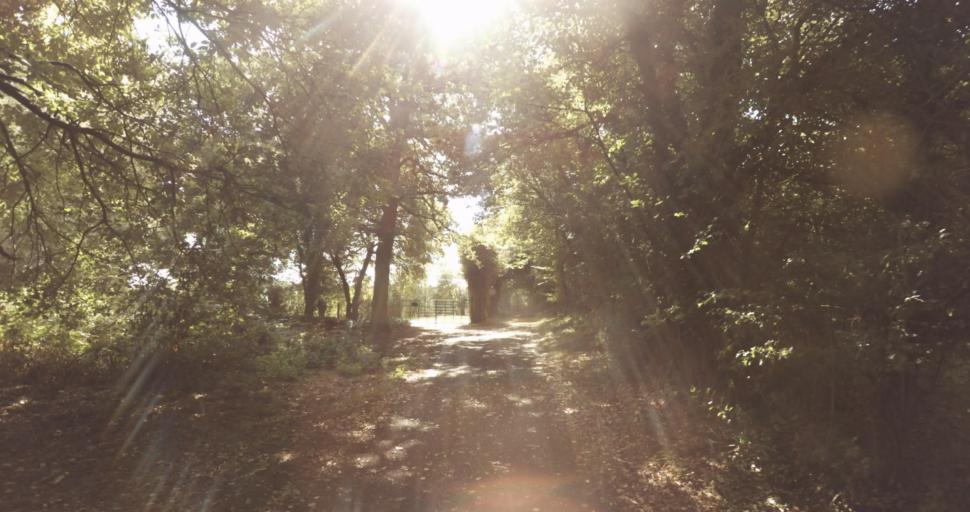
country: FR
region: Lower Normandy
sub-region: Departement du Calvados
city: Orbec
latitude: 48.9623
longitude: 0.3854
